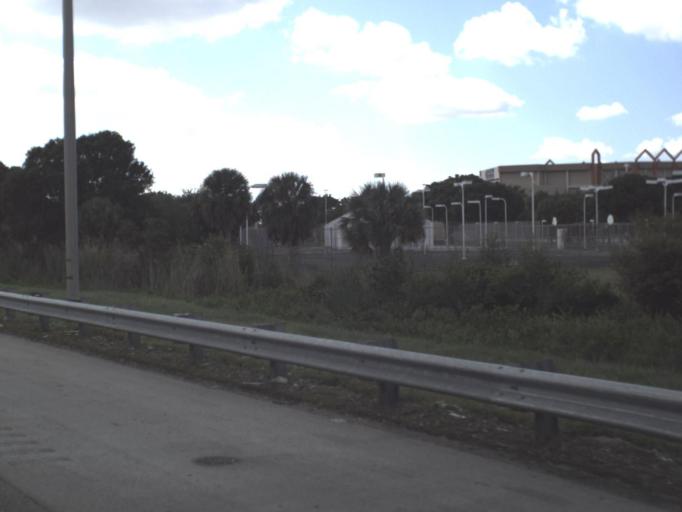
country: US
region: Florida
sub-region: Broward County
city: Coconut Creek
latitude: 26.2412
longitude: -80.1697
